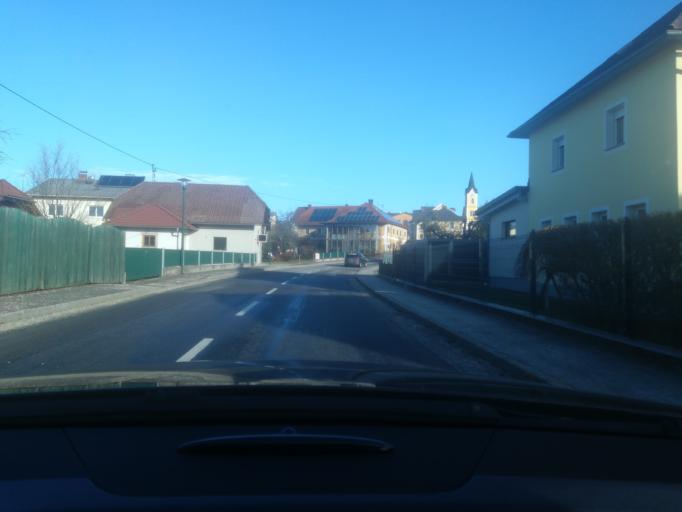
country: AT
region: Upper Austria
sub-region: Politischer Bezirk Urfahr-Umgebung
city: Herzogsdorf
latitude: 48.4289
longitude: 14.1104
